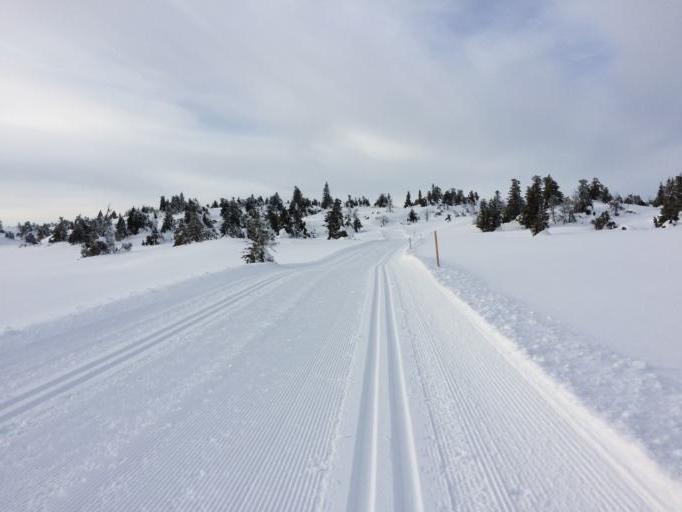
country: NO
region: Oppland
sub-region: Gausdal
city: Segalstad bru
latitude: 61.3254
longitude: 10.0392
